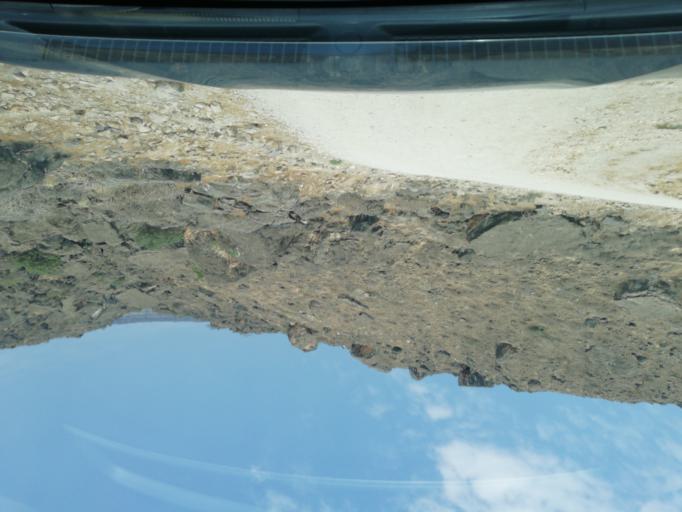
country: OM
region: Zufar
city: Salalah
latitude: 16.8210
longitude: 53.6962
